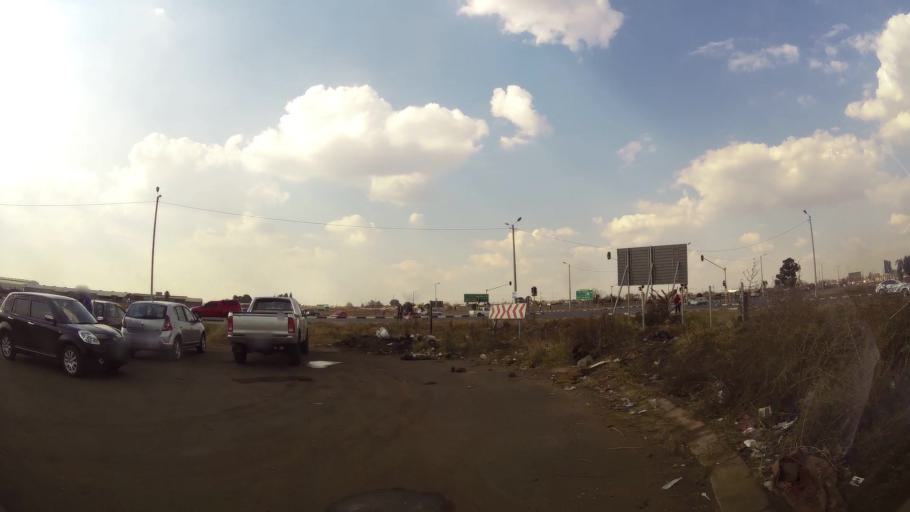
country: ZA
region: Gauteng
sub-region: Ekurhuleni Metropolitan Municipality
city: Germiston
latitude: -26.3118
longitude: 28.2022
